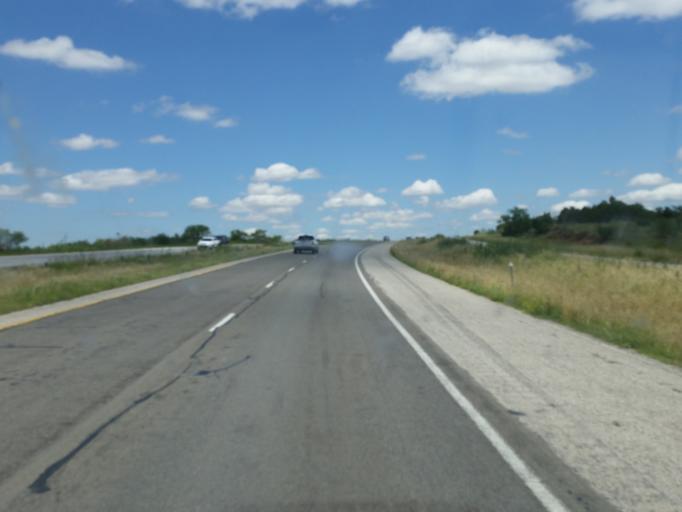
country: US
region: Texas
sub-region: Nolan County
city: Sweetwater
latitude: 32.4962
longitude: -100.2675
